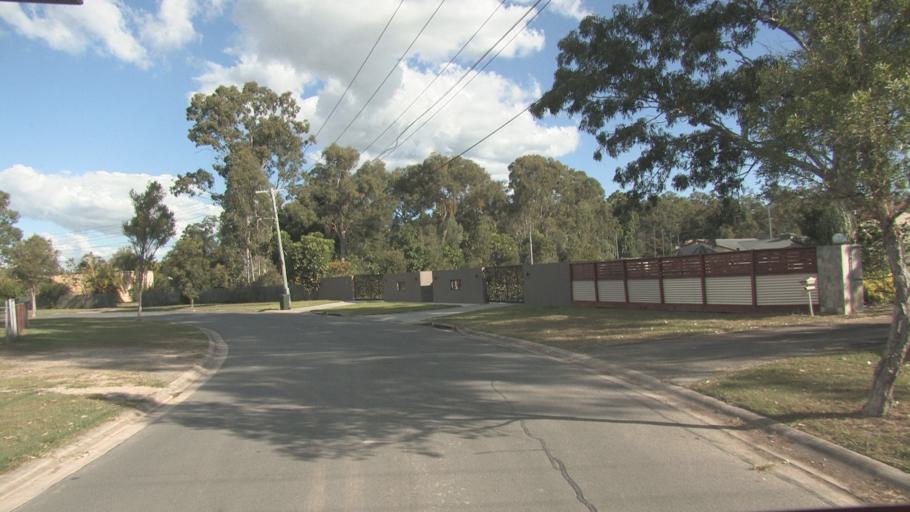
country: AU
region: Queensland
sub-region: Logan
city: Beenleigh
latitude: -27.6701
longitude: 153.2050
